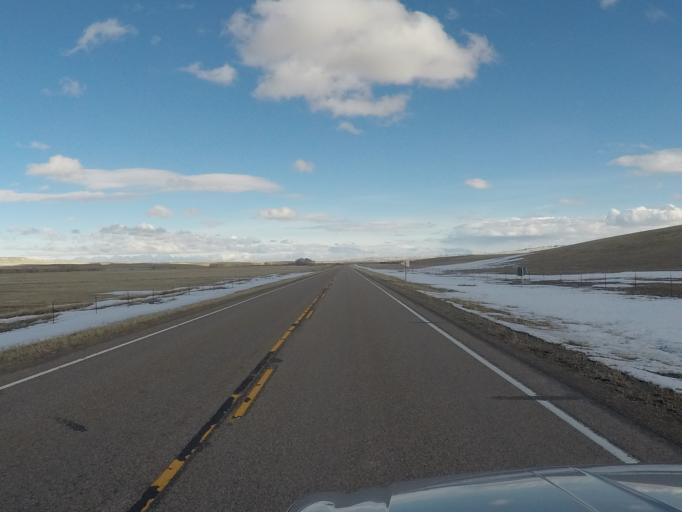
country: US
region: Montana
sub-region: Wheatland County
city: Harlowton
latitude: 46.4998
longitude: -110.3571
